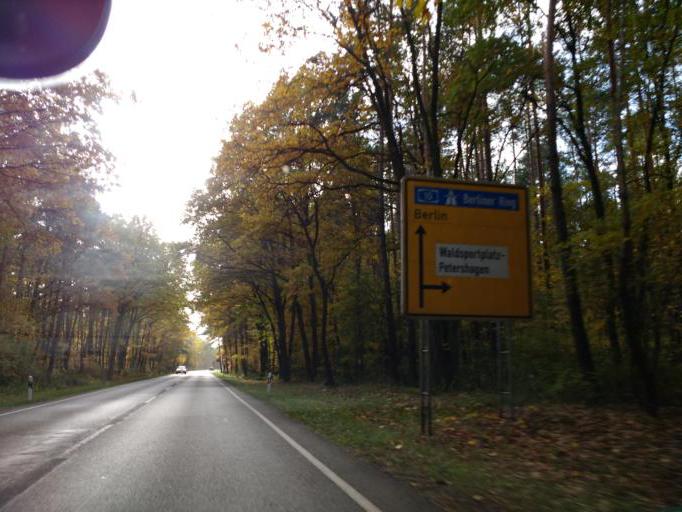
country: DE
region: Brandenburg
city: Petershagen
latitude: 52.5193
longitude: 13.8101
